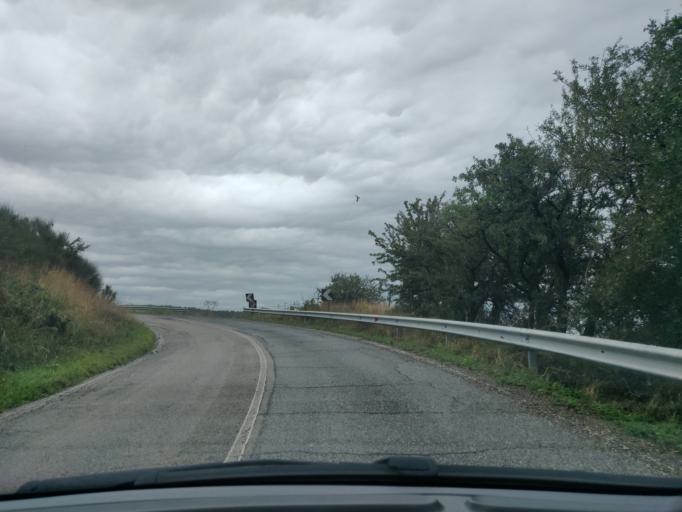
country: IT
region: Latium
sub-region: Citta metropolitana di Roma Capitale
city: Aurelia
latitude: 42.1314
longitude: 11.8419
